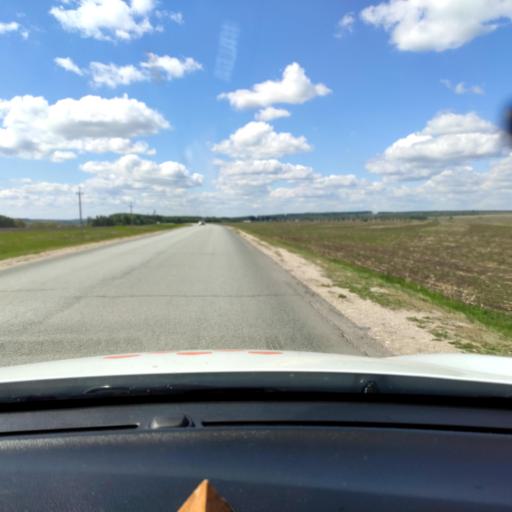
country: RU
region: Tatarstan
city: Kuybyshevskiy Zaton
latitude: 55.1684
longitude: 49.2113
